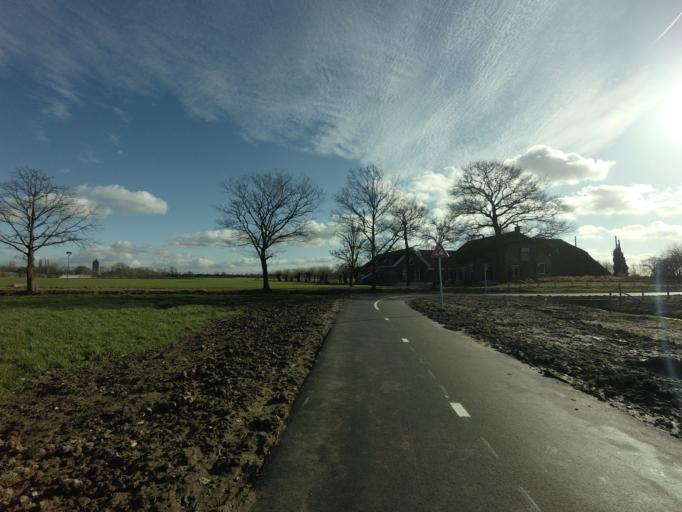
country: NL
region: Utrecht
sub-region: Stichtse Vecht
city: Spechtenkamp
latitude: 52.1074
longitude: 4.9858
